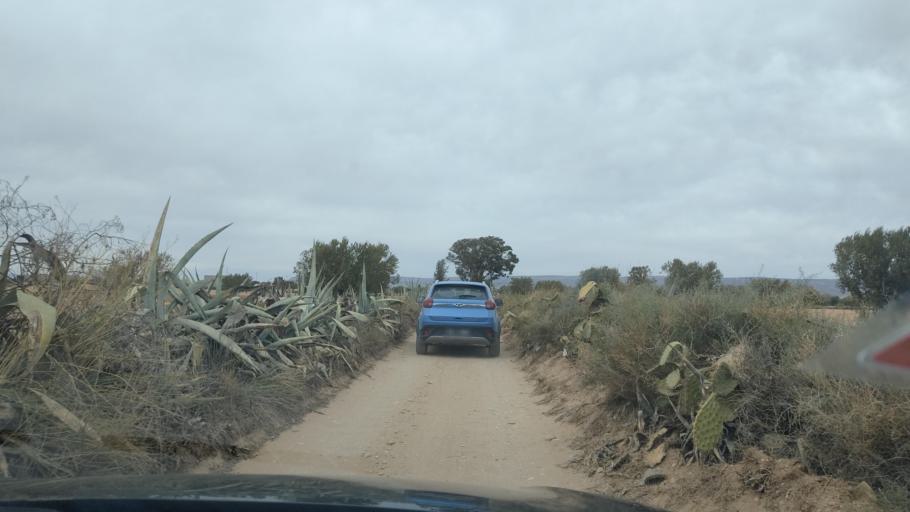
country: TN
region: Al Qasrayn
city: Kasserine
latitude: 35.2278
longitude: 8.9306
